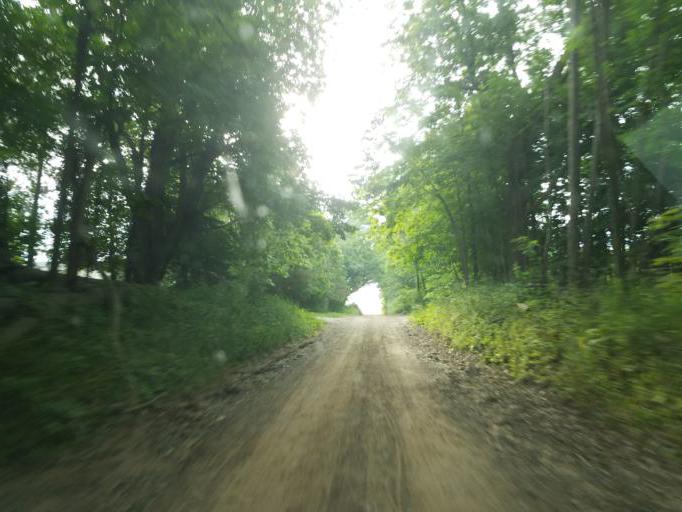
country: US
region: Michigan
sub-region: Eaton County
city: Charlotte
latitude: 42.6118
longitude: -84.9590
